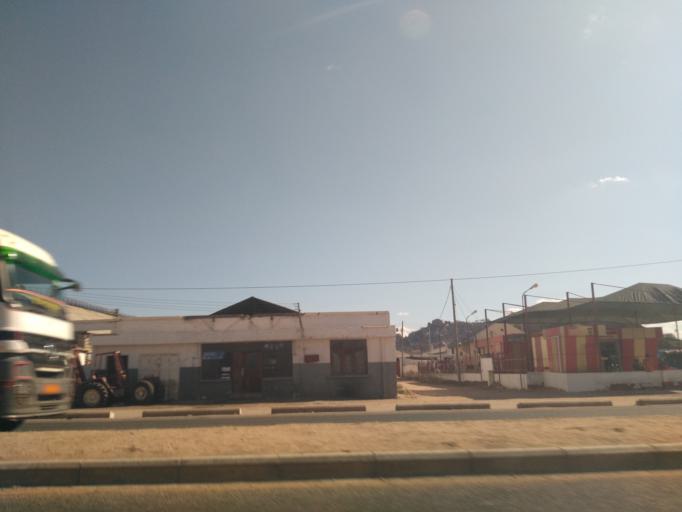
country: TZ
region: Dodoma
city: Dodoma
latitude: -6.1695
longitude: 35.7276
